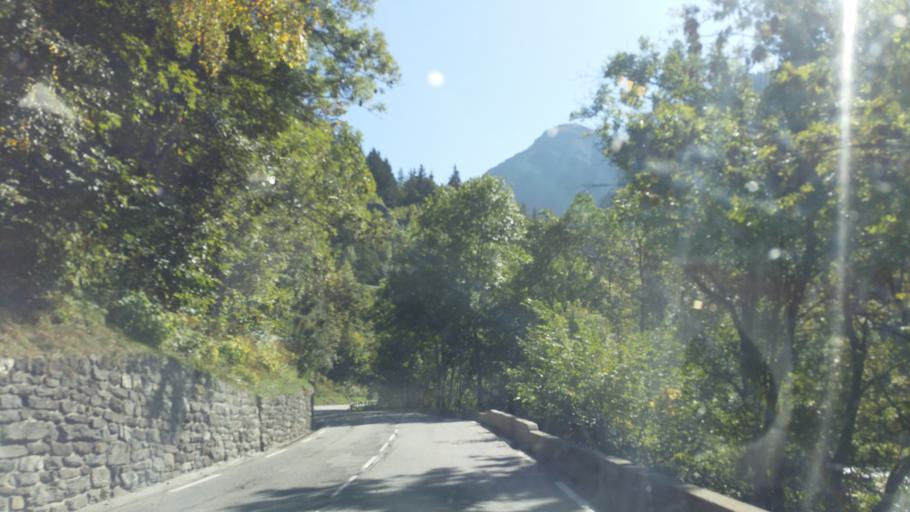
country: FR
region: Rhone-Alpes
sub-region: Departement de la Savoie
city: Seez
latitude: 45.5807
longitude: 6.8838
